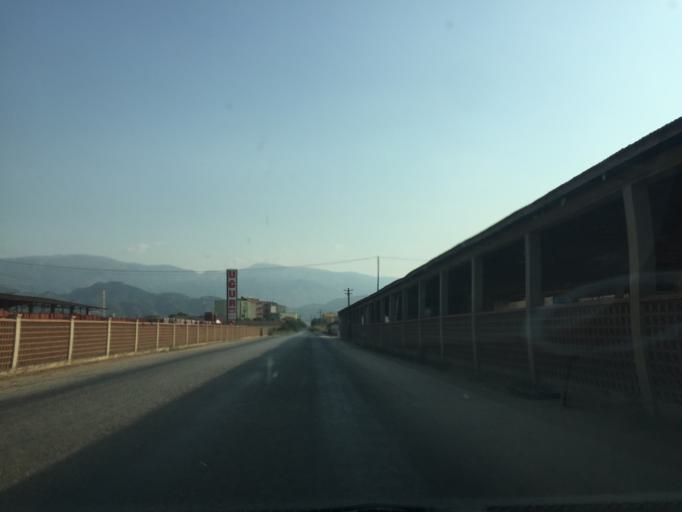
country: TR
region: Manisa
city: Salihli
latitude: 38.4990
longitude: 28.1838
